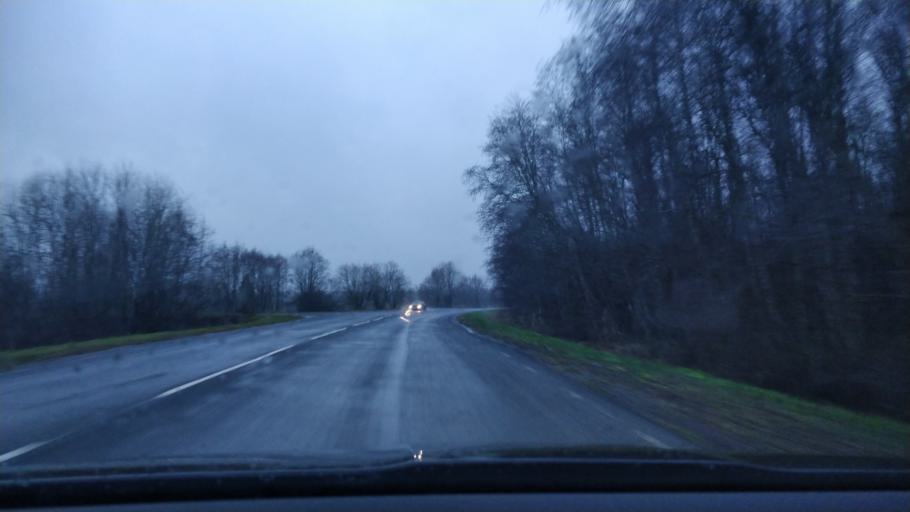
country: EE
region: Laeaene
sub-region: Lihula vald
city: Lihula
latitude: 58.7074
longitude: 23.8622
